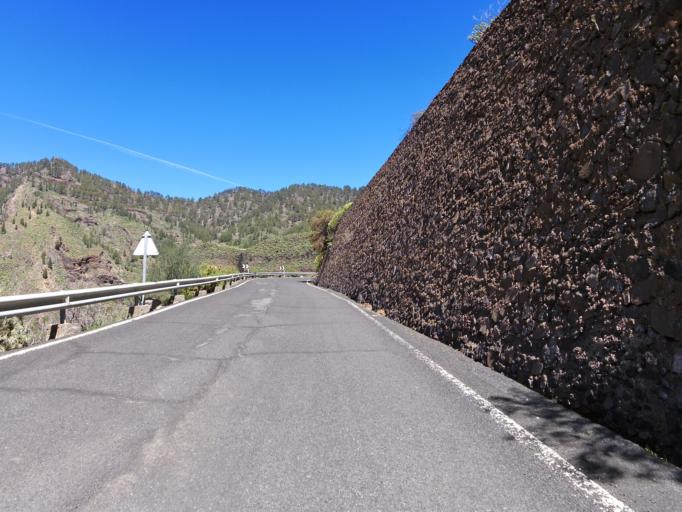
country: ES
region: Canary Islands
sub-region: Provincia de Las Palmas
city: Artenara
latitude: 28.0095
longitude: -15.6884
